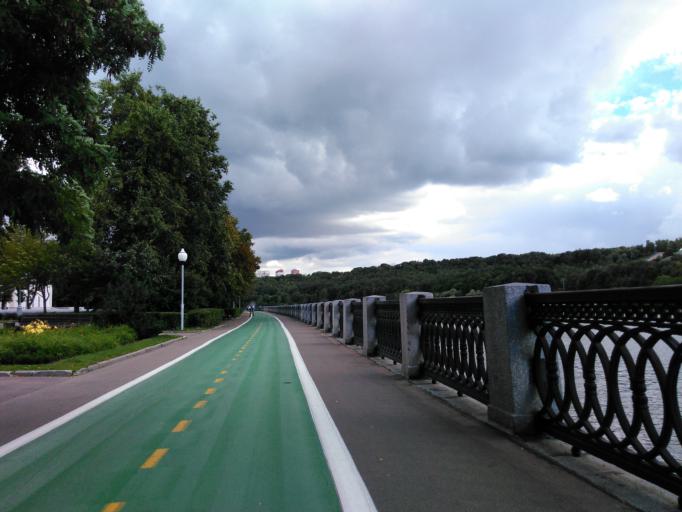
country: RU
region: Moscow
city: Luzhniki
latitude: 55.7159
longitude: 37.5454
